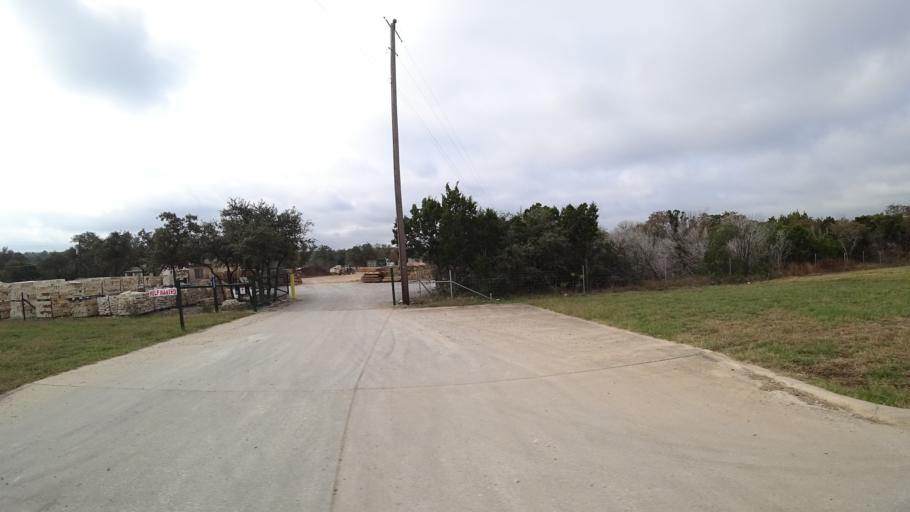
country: US
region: Texas
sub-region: Williamson County
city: Anderson Mill
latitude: 30.4598
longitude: -97.8380
